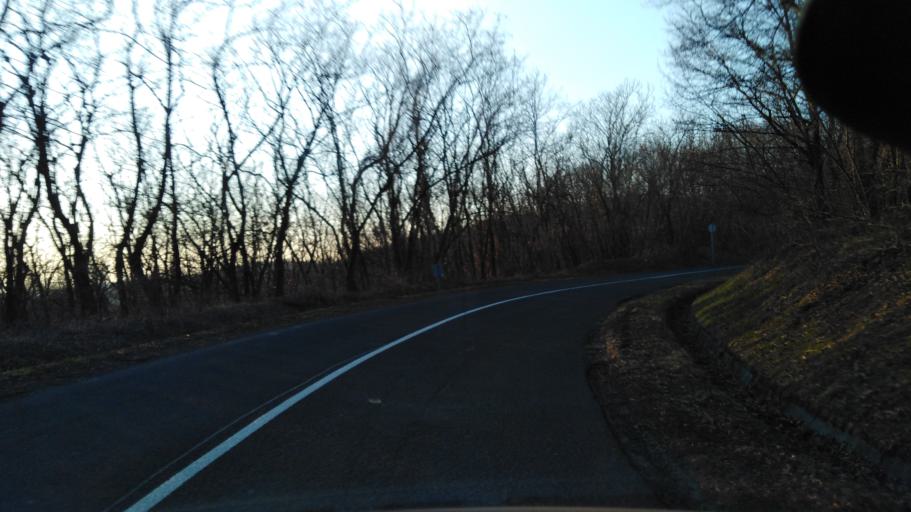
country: HU
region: Nograd
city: Salgotarjan
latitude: 48.0701
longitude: 19.8171
